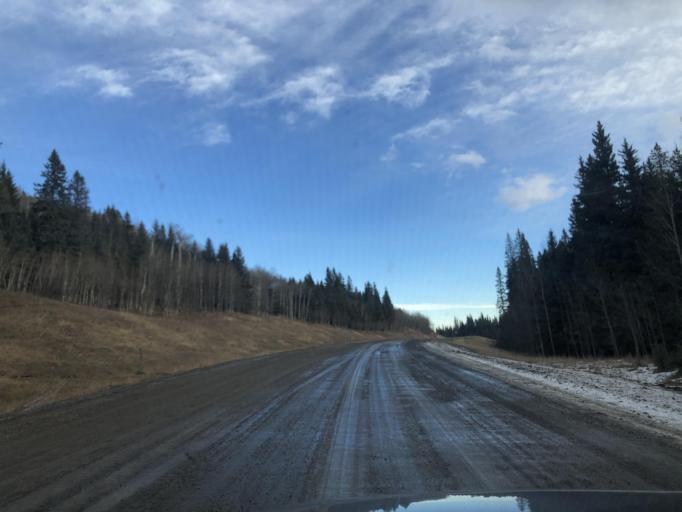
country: CA
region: Alberta
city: Cochrane
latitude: 51.0431
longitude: -114.7532
